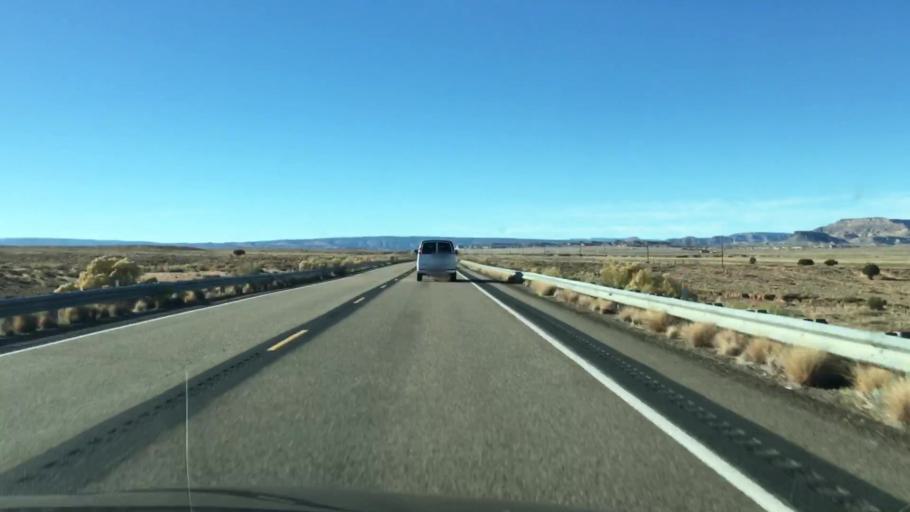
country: US
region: Arizona
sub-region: Coconino County
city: Page
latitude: 37.0981
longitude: -111.7815
